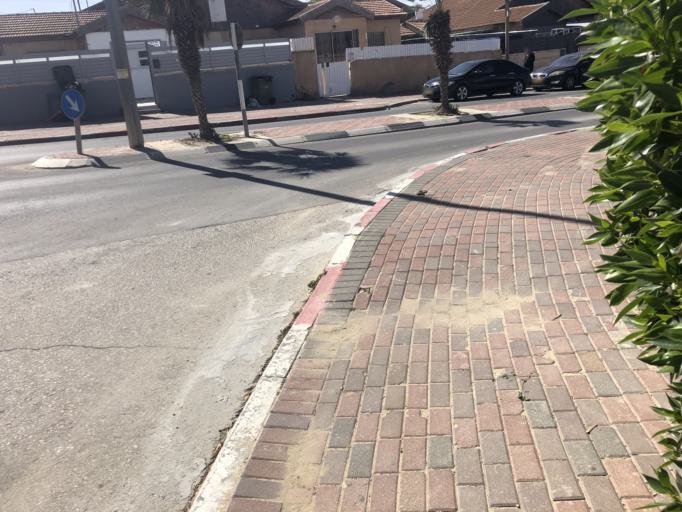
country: IL
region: Southern District
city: Dimona
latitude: 31.0664
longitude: 35.0410
